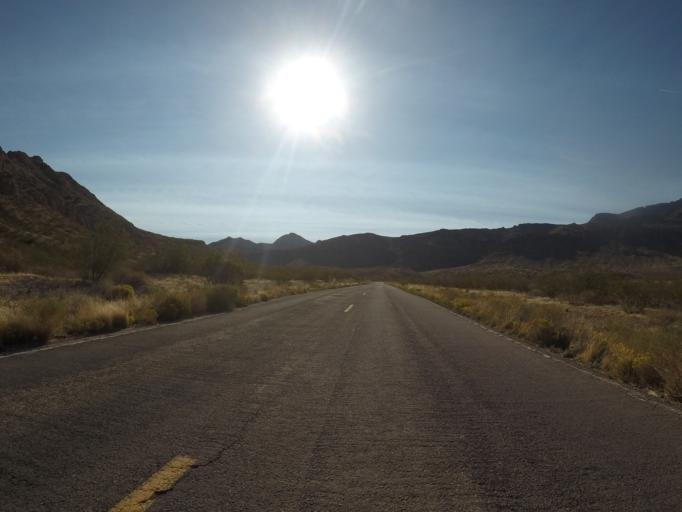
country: US
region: Nevada
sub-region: Clark County
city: Moapa Valley
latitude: 36.4186
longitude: -114.6189
